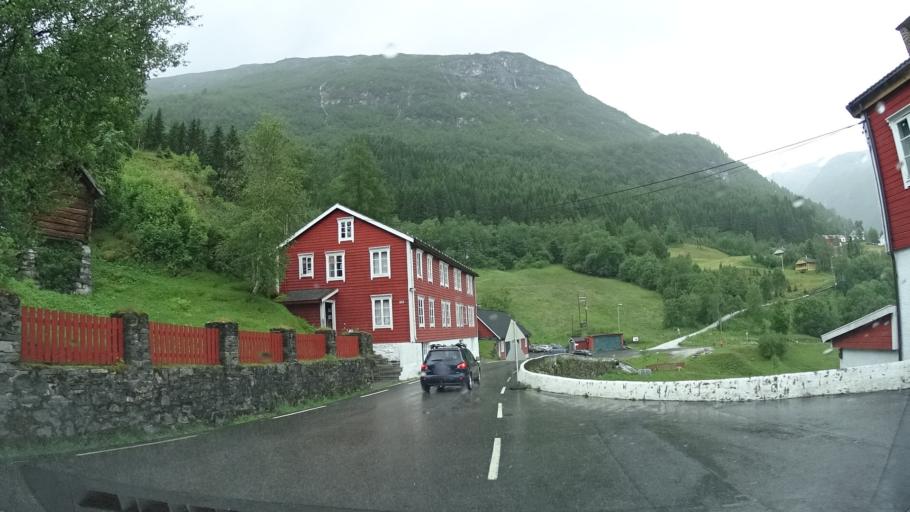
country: NO
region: Sogn og Fjordane
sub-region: Vik
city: Vik
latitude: 60.8353
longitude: 6.6806
